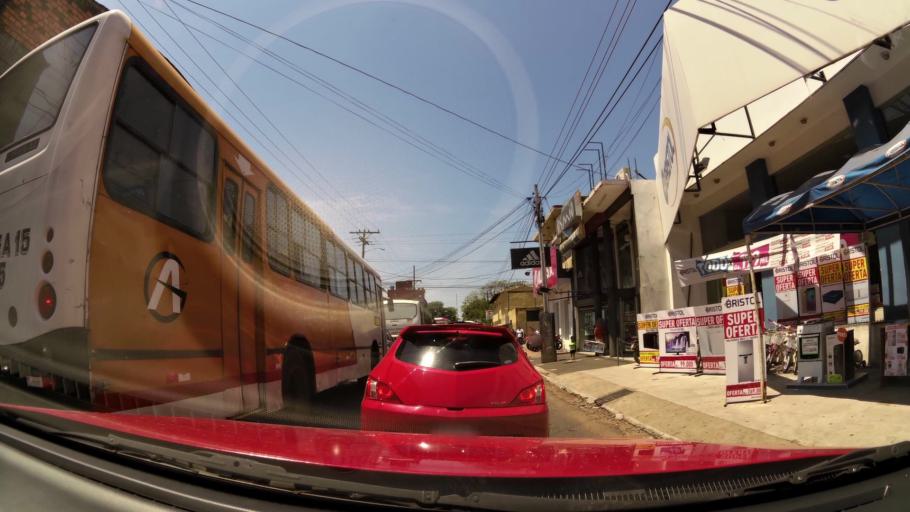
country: PY
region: Central
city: Nemby
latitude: -25.3937
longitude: -57.5458
